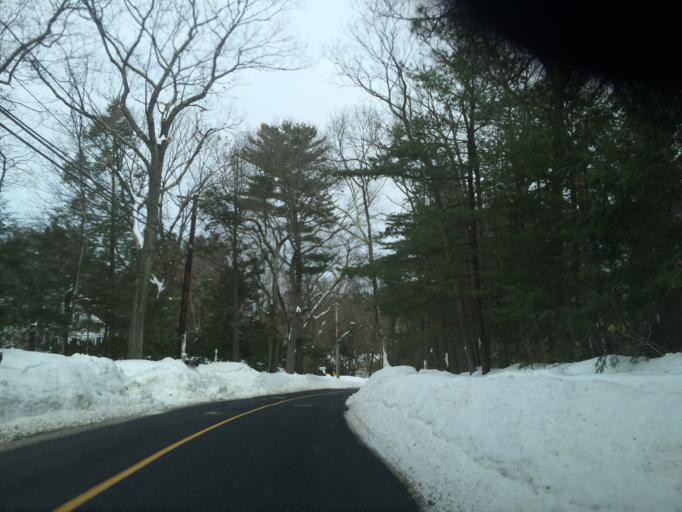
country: US
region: Massachusetts
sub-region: Middlesex County
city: Weston
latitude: 42.3446
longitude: -71.2983
